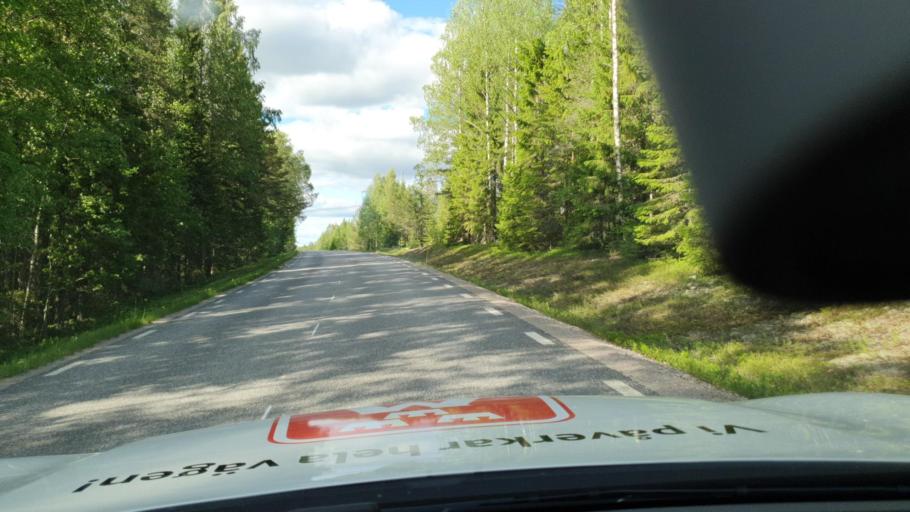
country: SE
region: Vaesterbotten
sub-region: Vannas Kommun
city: Vannasby
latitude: 63.8094
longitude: 19.8556
